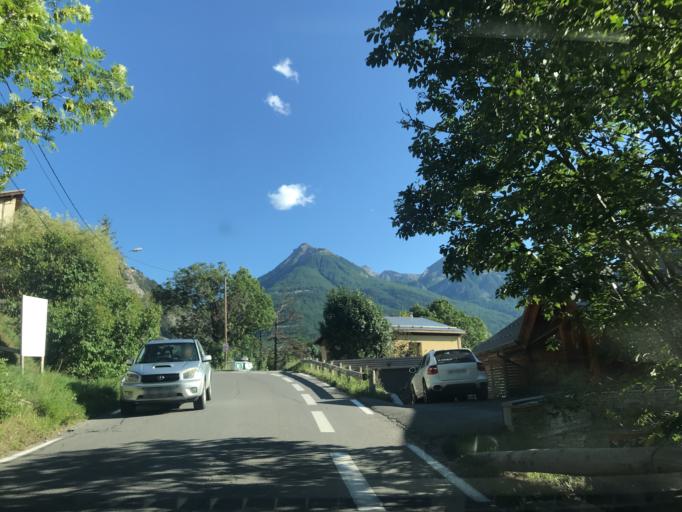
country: FR
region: Provence-Alpes-Cote d'Azur
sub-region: Departement des Hautes-Alpes
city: Briancon
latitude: 44.8901
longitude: 6.6390
